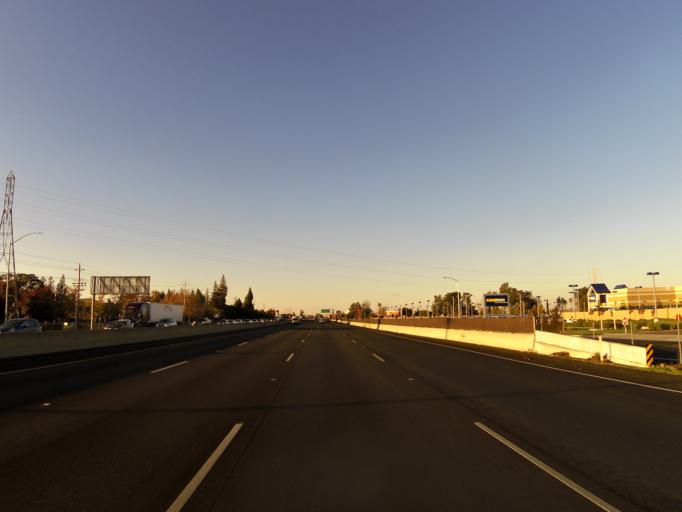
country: US
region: California
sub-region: Sacramento County
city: Florin
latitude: 38.4604
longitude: -121.4121
